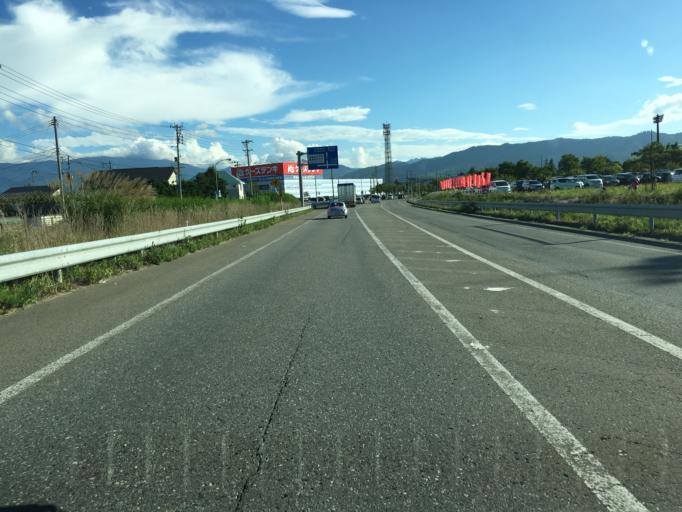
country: JP
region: Yamagata
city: Yonezawa
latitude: 37.9287
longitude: 140.1088
